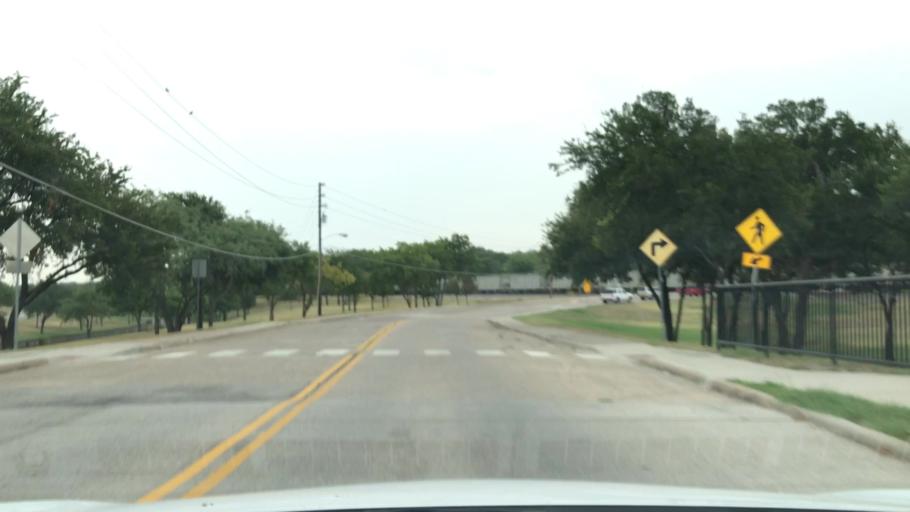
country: US
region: Texas
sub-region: Dallas County
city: Carrollton
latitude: 32.9652
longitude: -96.8984
